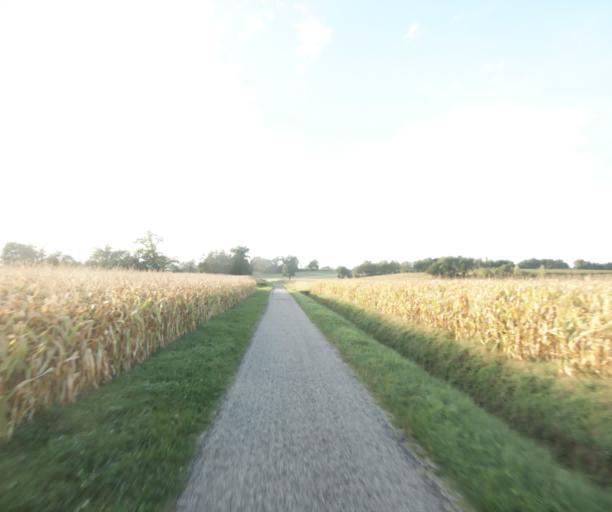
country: FR
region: Midi-Pyrenees
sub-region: Departement du Gers
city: Le Houga
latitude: 43.8291
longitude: -0.1137
